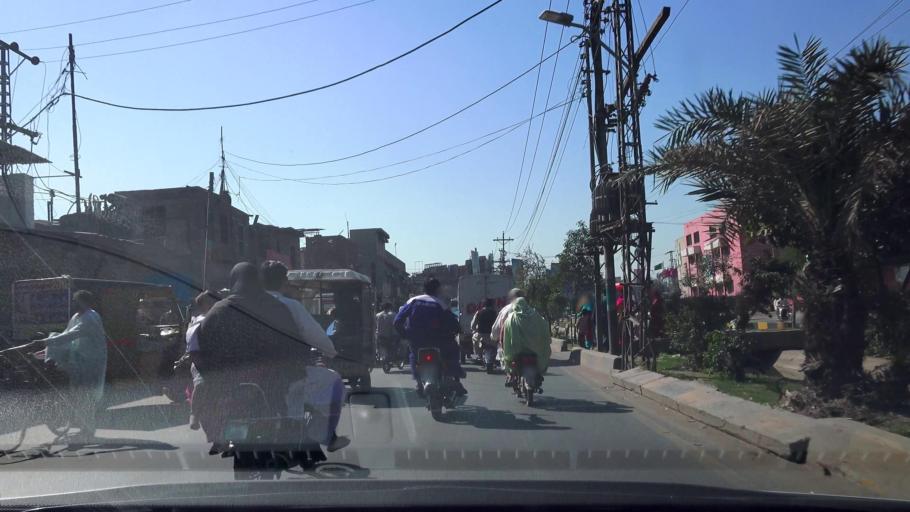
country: PK
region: Punjab
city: Faisalabad
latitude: 31.4127
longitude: 73.0671
